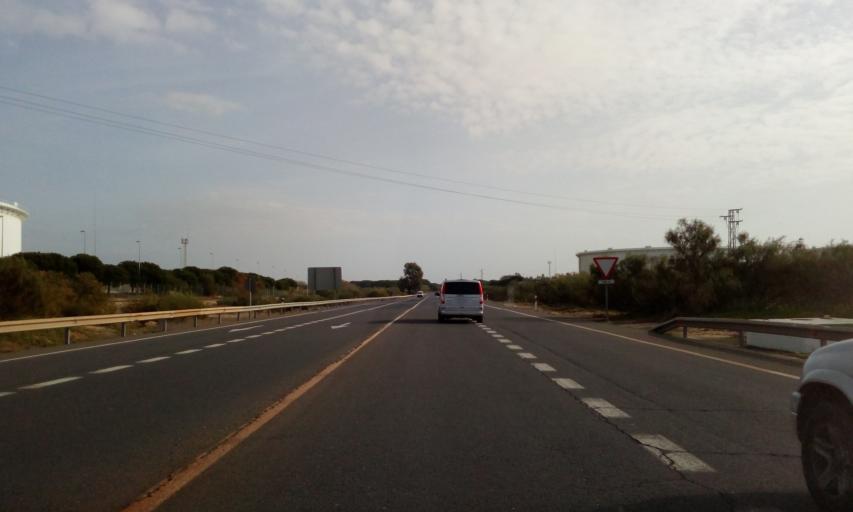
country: ES
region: Andalusia
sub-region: Provincia de Huelva
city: Palos de la Frontera
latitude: 37.1730
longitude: -6.8998
